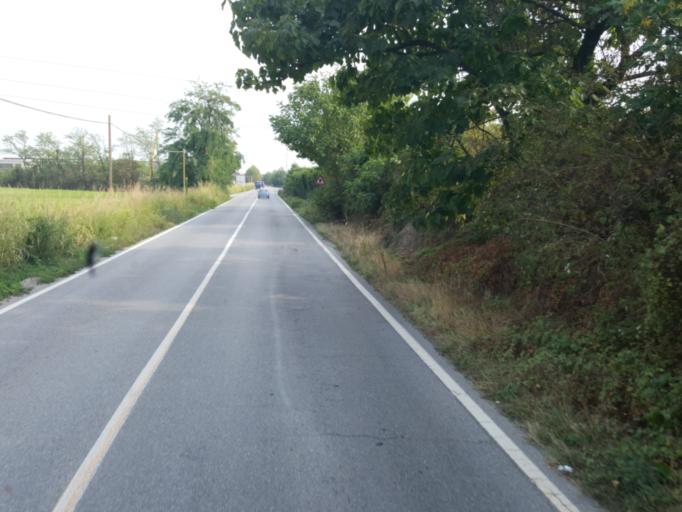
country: IT
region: Lombardy
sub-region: Provincia di Bergamo
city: Cavernago
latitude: 45.6414
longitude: 9.7538
